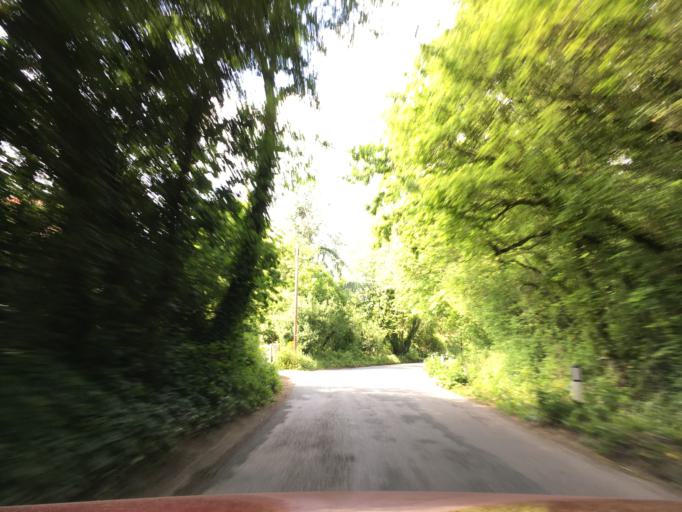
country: GB
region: England
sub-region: South Gloucestershire
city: Alveston
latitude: 51.6097
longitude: -2.5490
